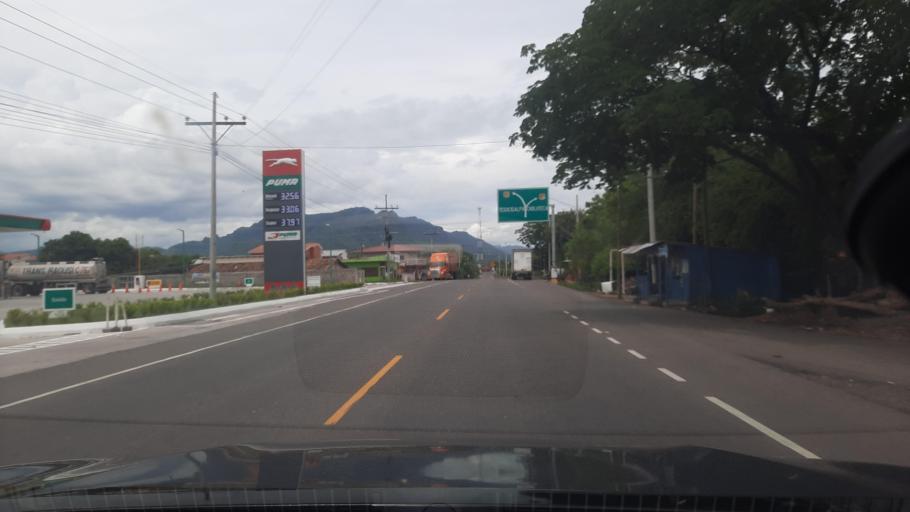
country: HN
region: Valle
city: Jicaro Galan
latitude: 13.5318
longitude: -87.4435
